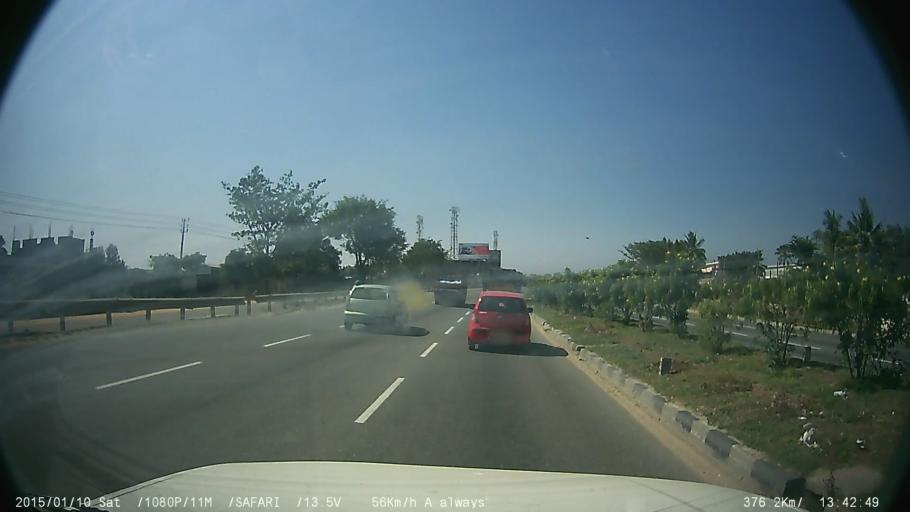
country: IN
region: Karnataka
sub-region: Bangalore Urban
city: Anekal
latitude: 12.7871
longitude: 77.7394
